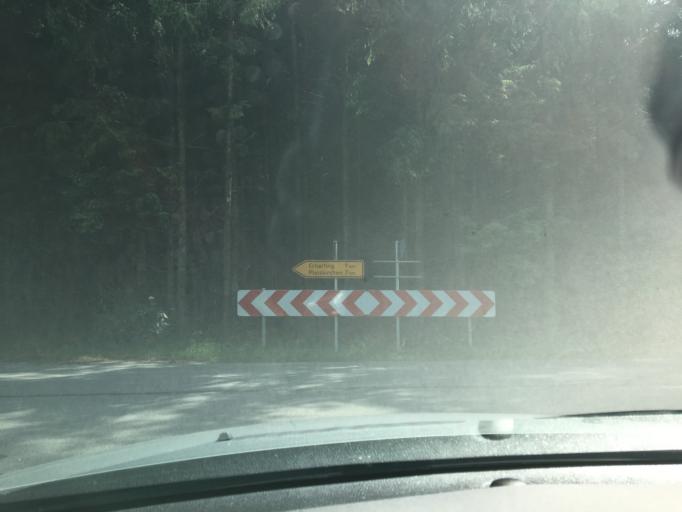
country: DE
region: Bavaria
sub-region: Upper Bavaria
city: Niedertaufkirchen
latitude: 48.3475
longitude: 12.5703
